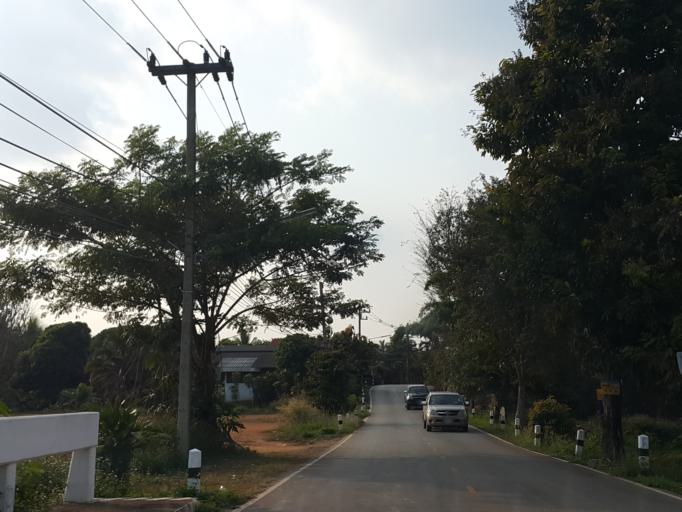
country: TH
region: Chiang Mai
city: Mae On
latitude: 18.9081
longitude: 99.2420
